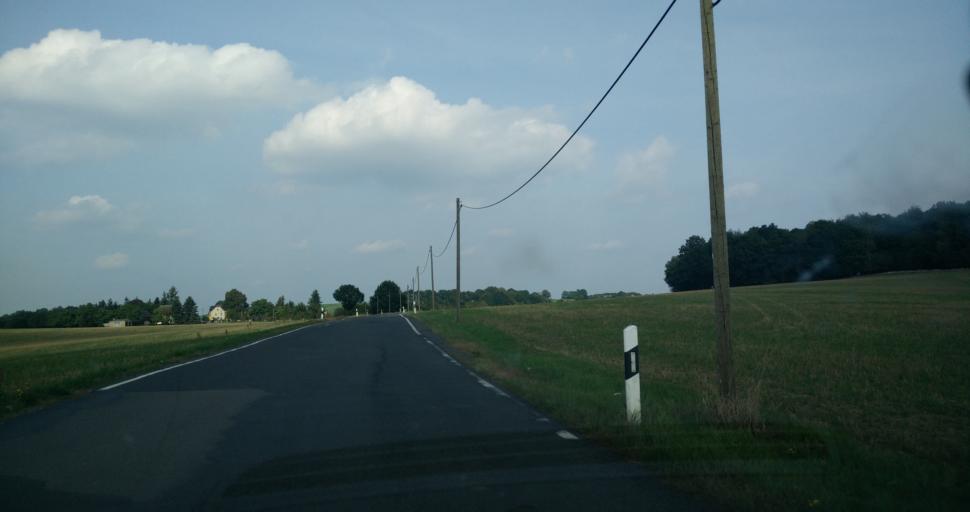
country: DE
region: Saxony
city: Rochlitz
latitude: 51.0834
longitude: 12.7932
